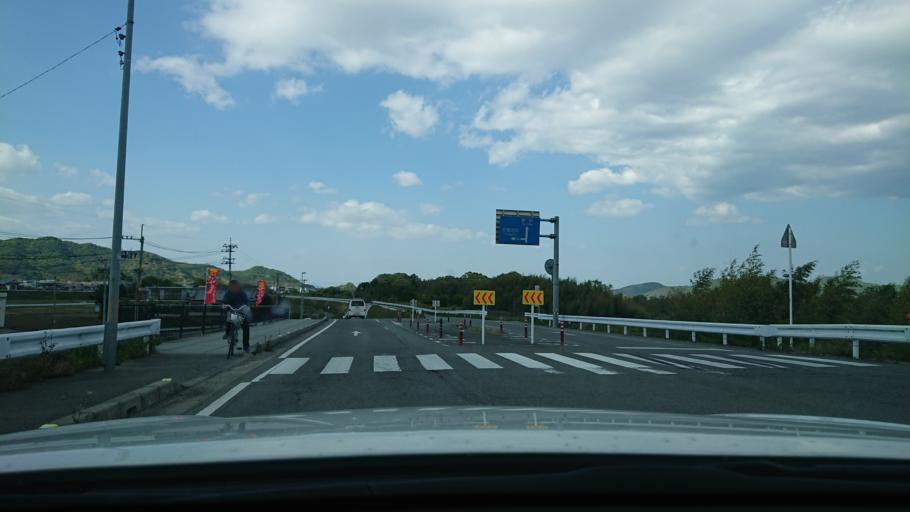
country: JP
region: Tokushima
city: Komatsushimacho
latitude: 33.9952
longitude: 134.5473
